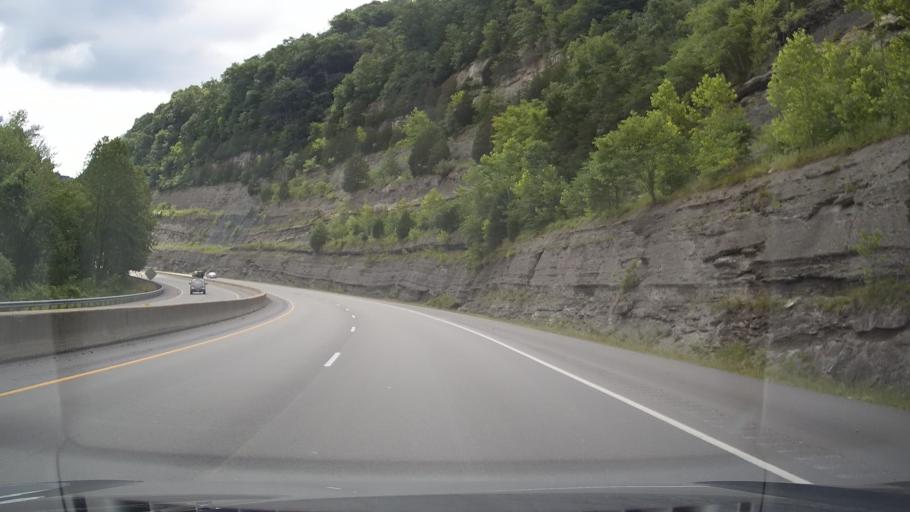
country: US
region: Kentucky
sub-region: Floyd County
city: Prestonsburg
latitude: 37.5944
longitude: -82.6654
